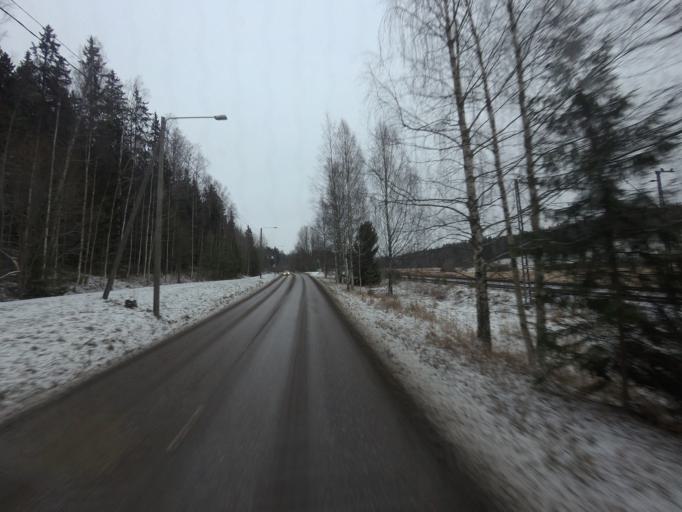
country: FI
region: Uusimaa
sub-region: Helsinki
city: Espoo
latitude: 60.1992
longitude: 24.6248
